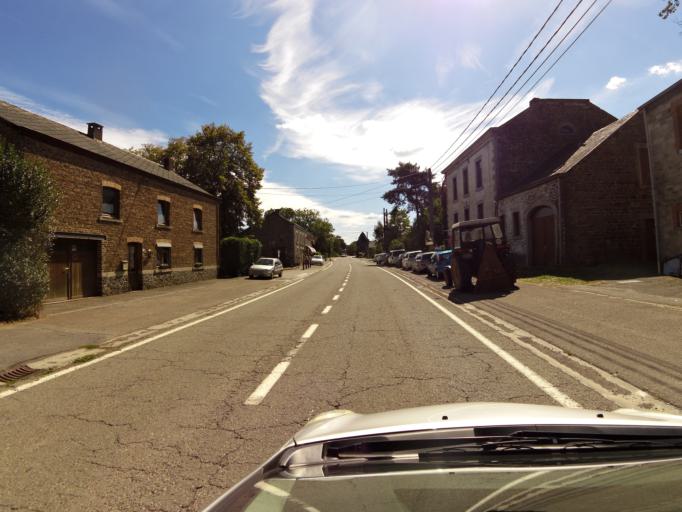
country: BE
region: Wallonia
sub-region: Province du Luxembourg
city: Rendeux
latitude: 50.2428
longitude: 5.4983
